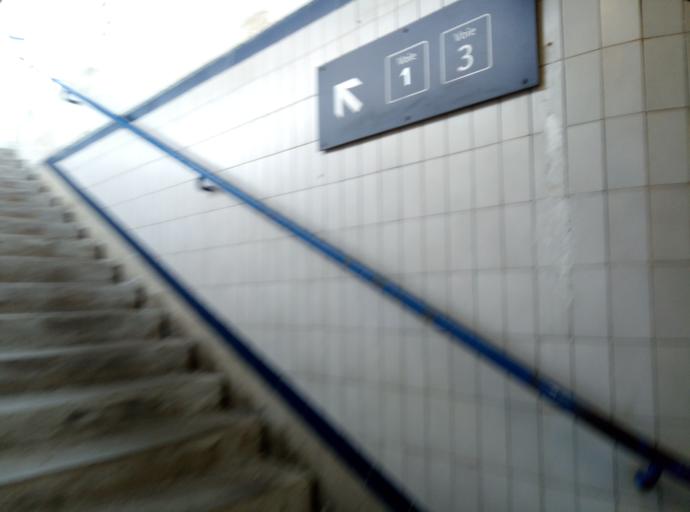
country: FR
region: Picardie
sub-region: Departement de l'Oise
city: Compiegne
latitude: 49.4225
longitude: 2.8234
